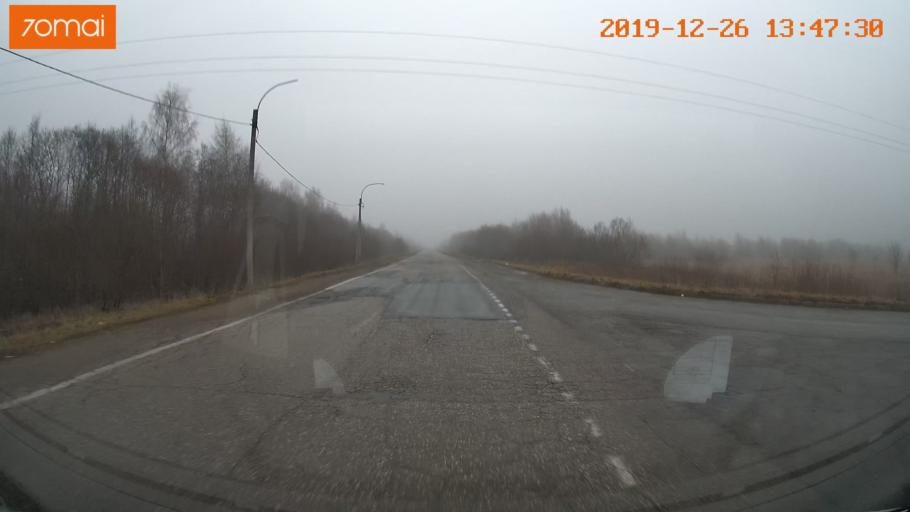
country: RU
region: Vologda
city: Sheksna
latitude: 58.6843
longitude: 38.5348
